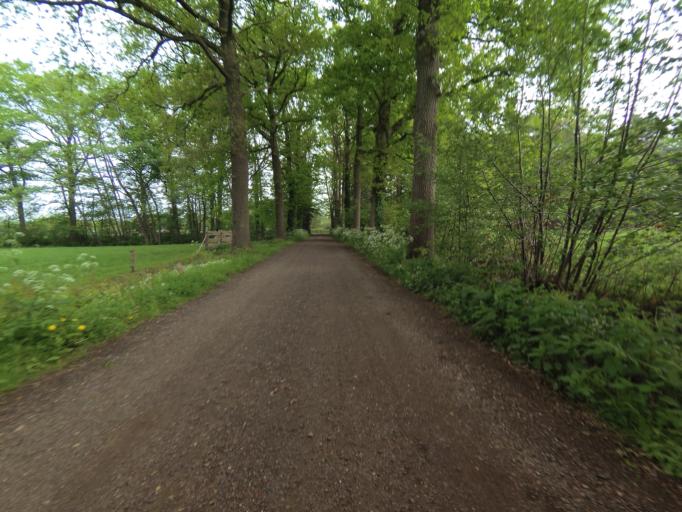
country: NL
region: Gelderland
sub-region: Gemeente Barneveld
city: Terschuur
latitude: 52.1494
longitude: 5.5323
